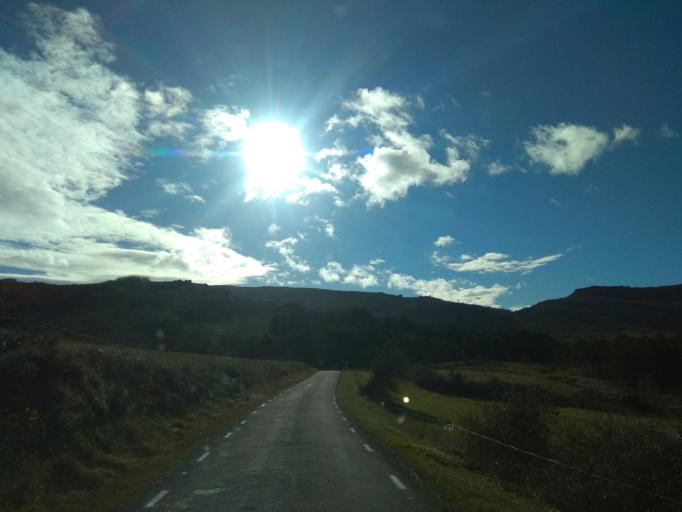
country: ES
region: Cantabria
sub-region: Provincia de Cantabria
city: San Martin de Elines
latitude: 42.9504
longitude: -3.8116
